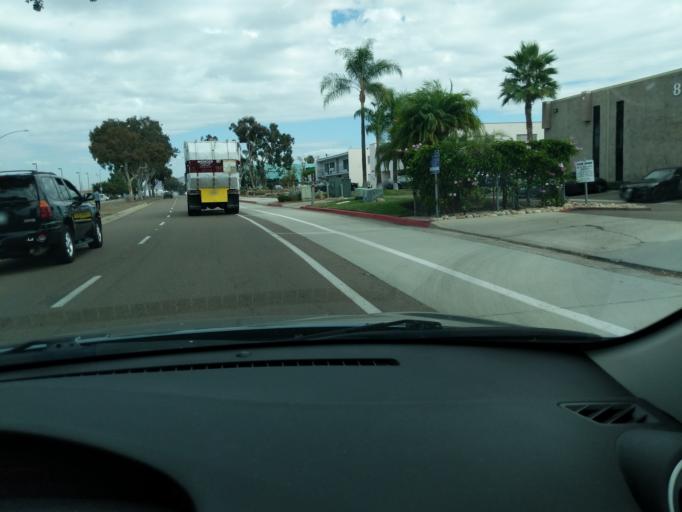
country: US
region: California
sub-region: San Diego County
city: San Diego
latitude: 32.8203
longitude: -117.1389
